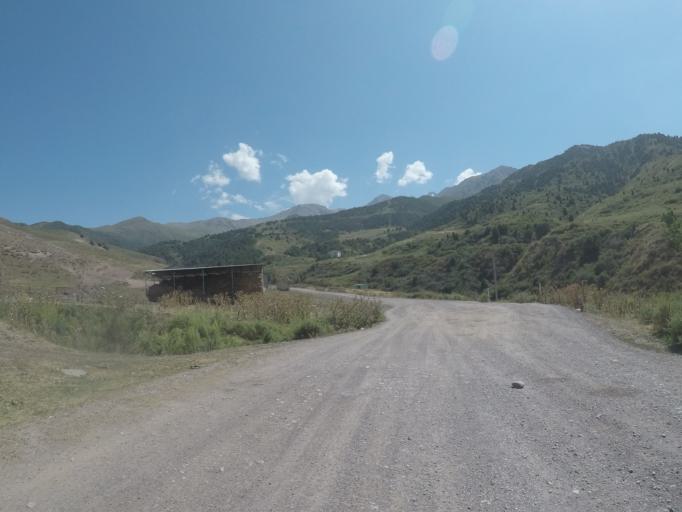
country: KG
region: Chuy
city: Bishkek
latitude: 42.6485
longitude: 74.5124
